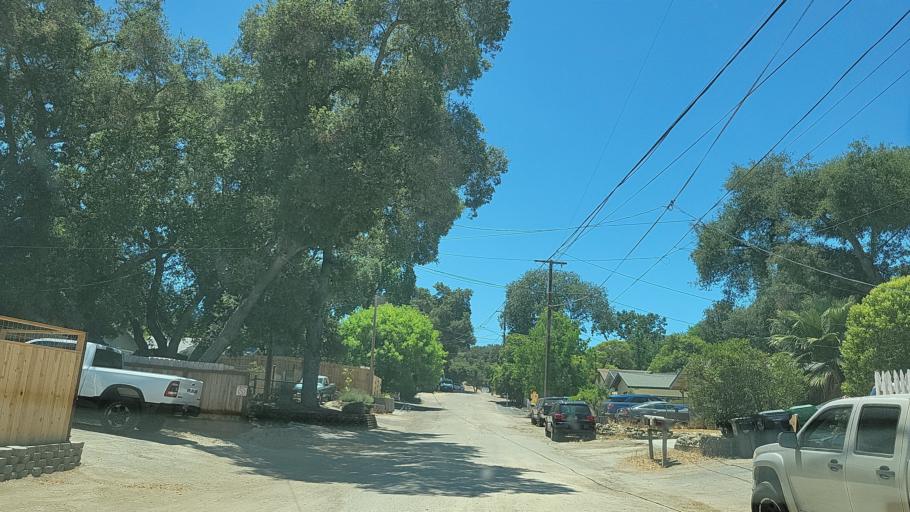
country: US
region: California
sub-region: San Luis Obispo County
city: Atascadero
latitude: 35.5064
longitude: -120.6732
